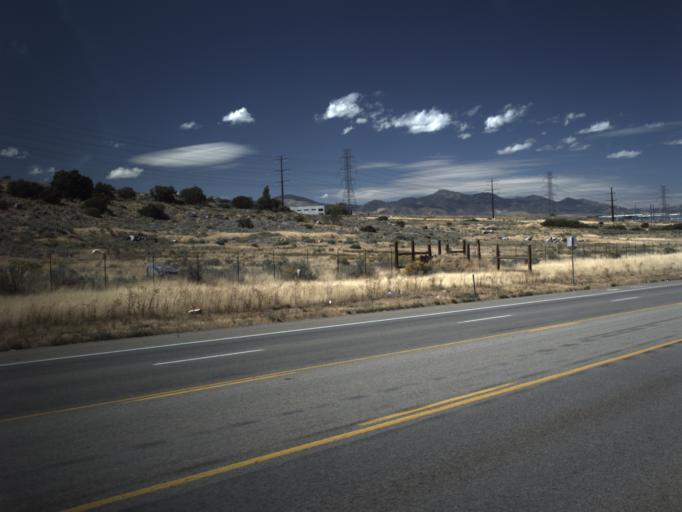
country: US
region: Utah
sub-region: Salt Lake County
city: Bluffdale
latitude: 40.4581
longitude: -111.9406
